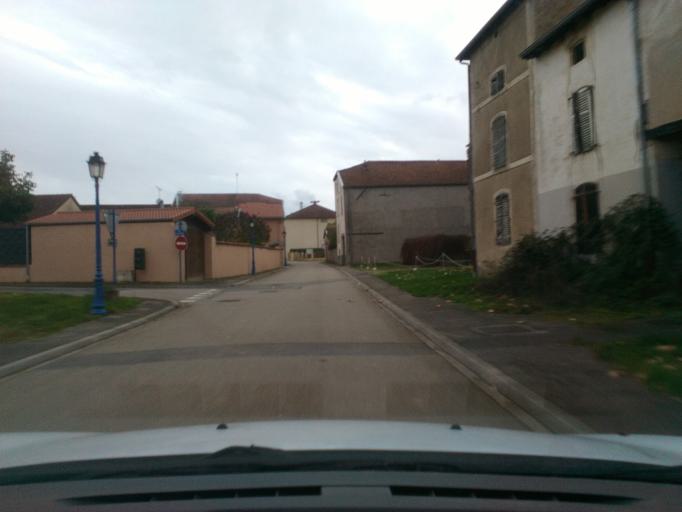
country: FR
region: Lorraine
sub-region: Departement des Vosges
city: Mirecourt
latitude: 48.3323
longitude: 6.0585
